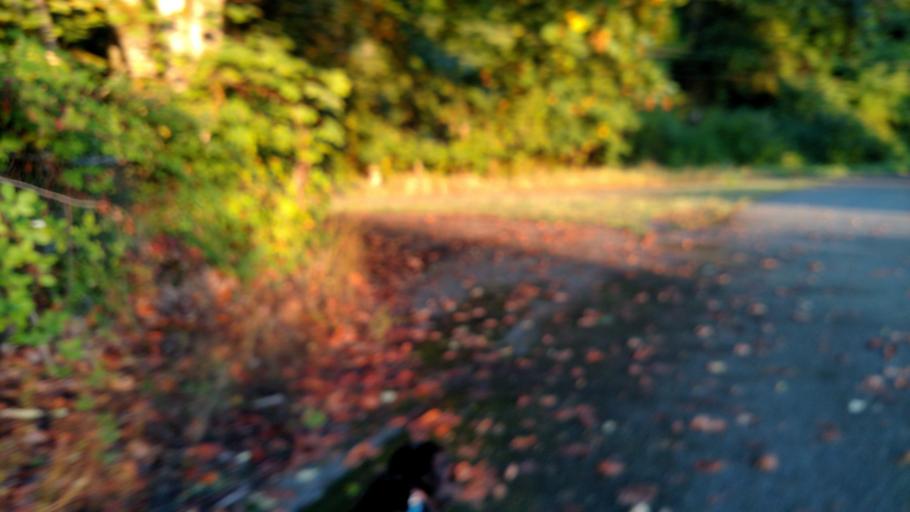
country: US
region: Washington
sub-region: King County
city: Kent
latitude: 47.3923
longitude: -122.2745
